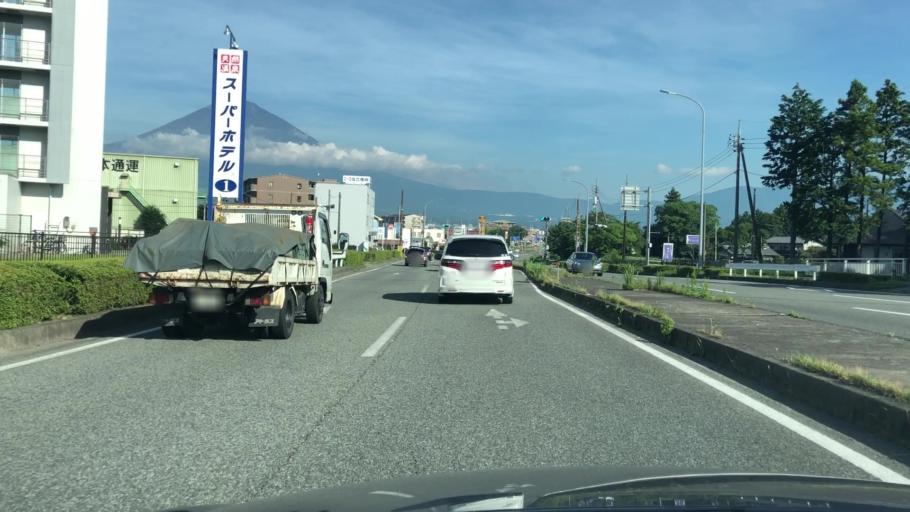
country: JP
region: Shizuoka
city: Gotemba
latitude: 35.2980
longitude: 138.9507
